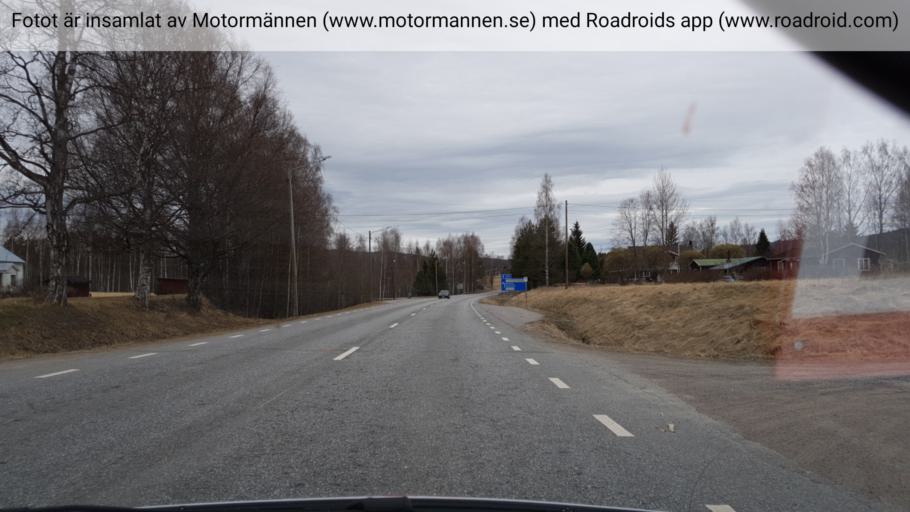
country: SE
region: Vaesternorrland
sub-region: Solleftea Kommun
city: Solleftea
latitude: 63.2398
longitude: 17.2082
